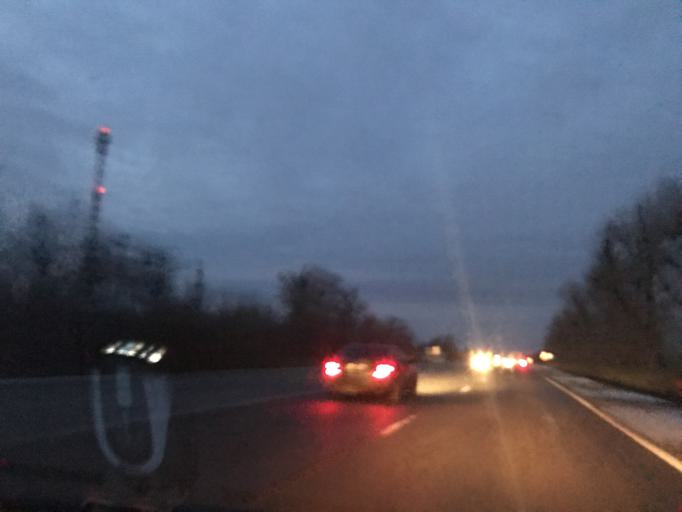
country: RU
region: Rostov
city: Bataysk
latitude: 47.0355
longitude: 39.7409
